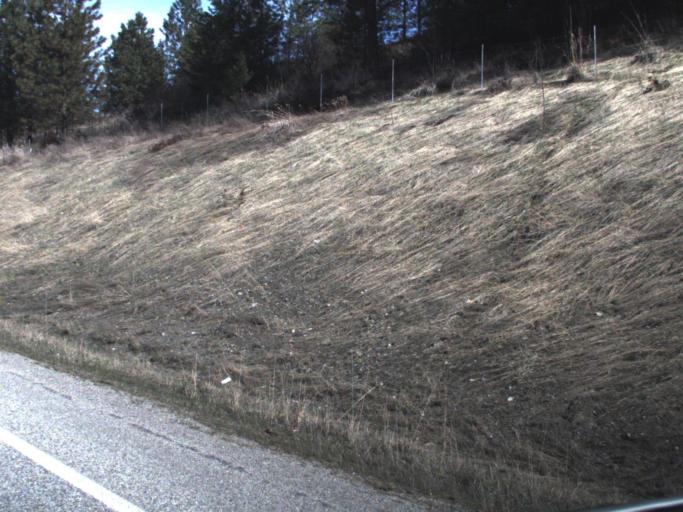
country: US
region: Washington
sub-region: Stevens County
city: Colville
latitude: 48.5191
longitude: -117.8101
